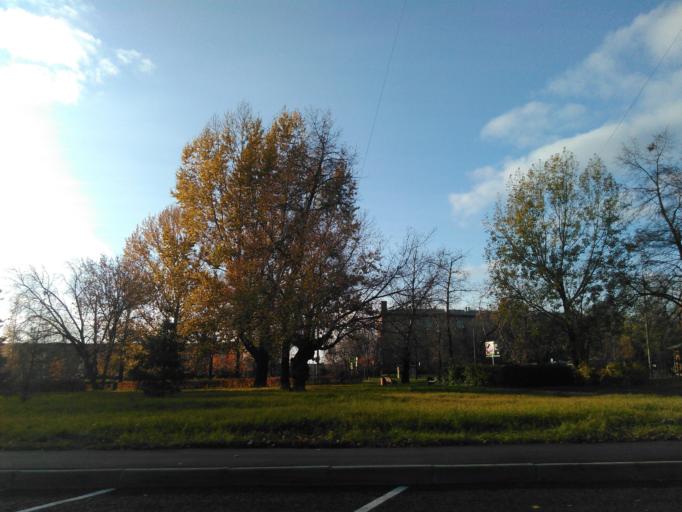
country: RU
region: Moscow
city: Mar'ina Roshcha
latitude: 55.8140
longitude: 37.6200
